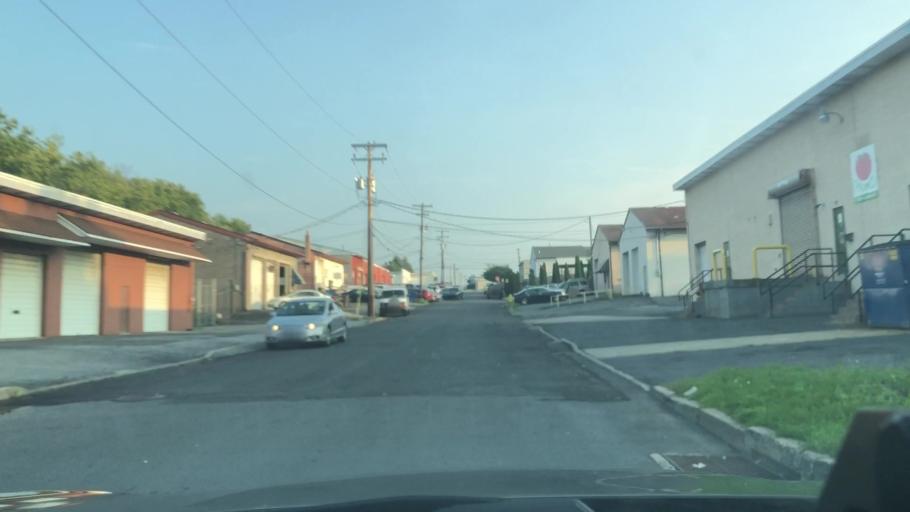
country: US
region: Pennsylvania
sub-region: Lehigh County
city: Fullerton
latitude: 40.6278
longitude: -75.4466
